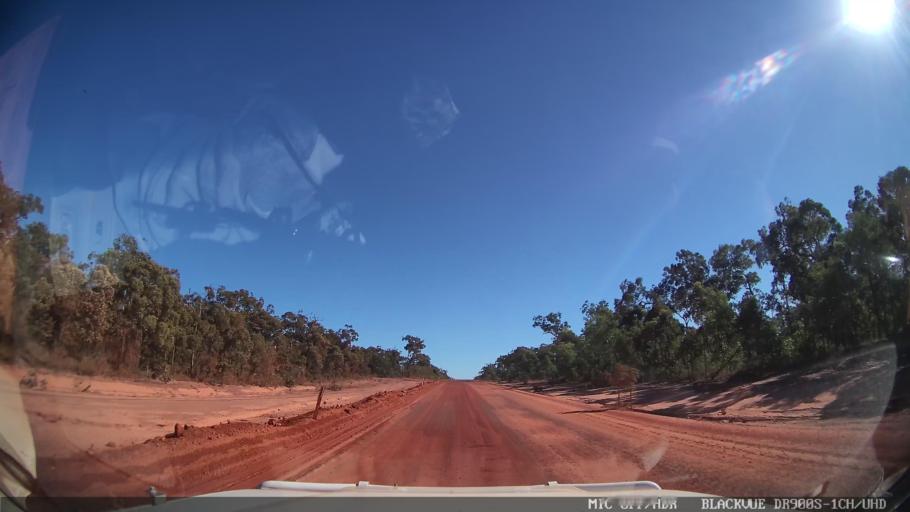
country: AU
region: Queensland
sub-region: Torres
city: Thursday Island
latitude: -11.3969
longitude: 142.3569
